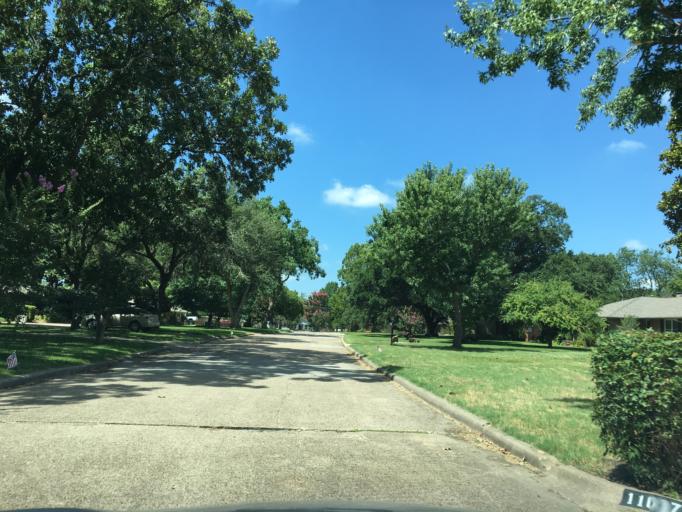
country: US
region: Texas
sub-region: Dallas County
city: Garland
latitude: 32.8383
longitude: -96.6521
